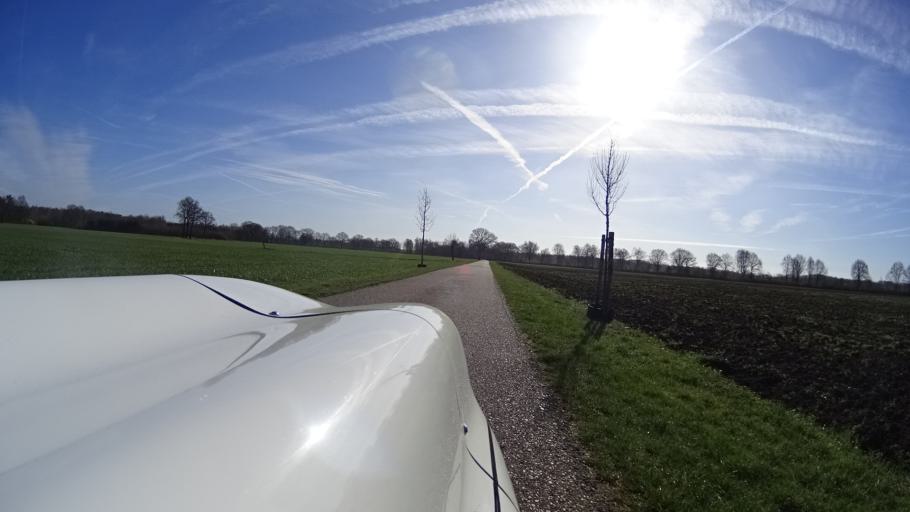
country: NL
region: North Brabant
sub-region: Gemeente Landerd
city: Zeeland
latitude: 51.6675
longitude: 5.6812
